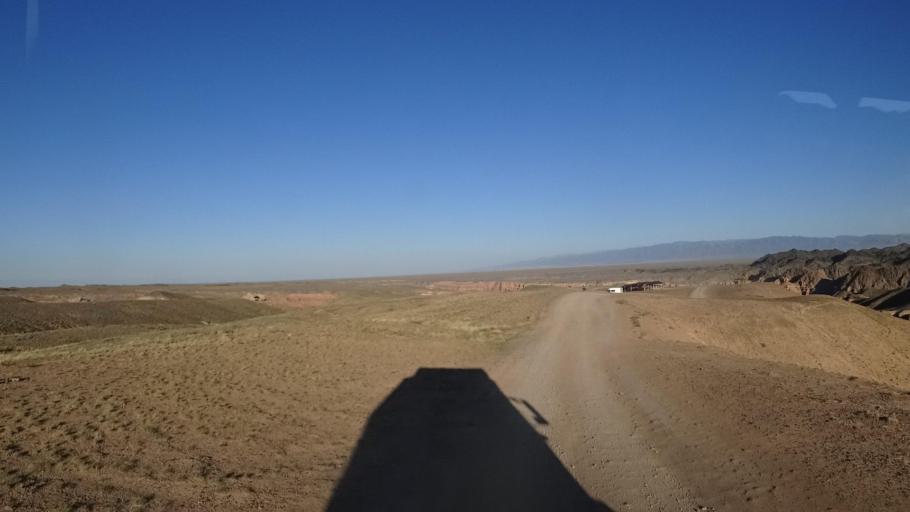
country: KZ
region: Almaty Oblysy
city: Kegen
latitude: 43.3555
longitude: 79.0594
